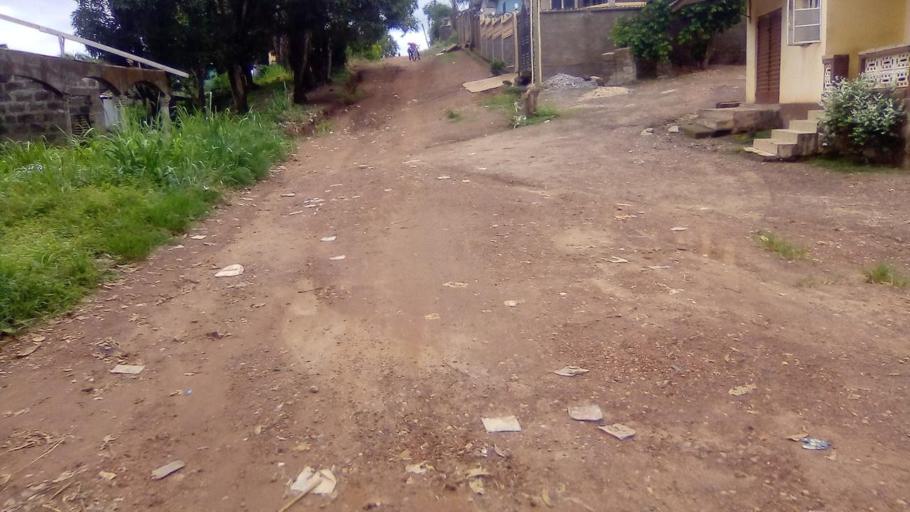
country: SL
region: Southern Province
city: Bo
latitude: 7.9434
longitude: -11.7417
